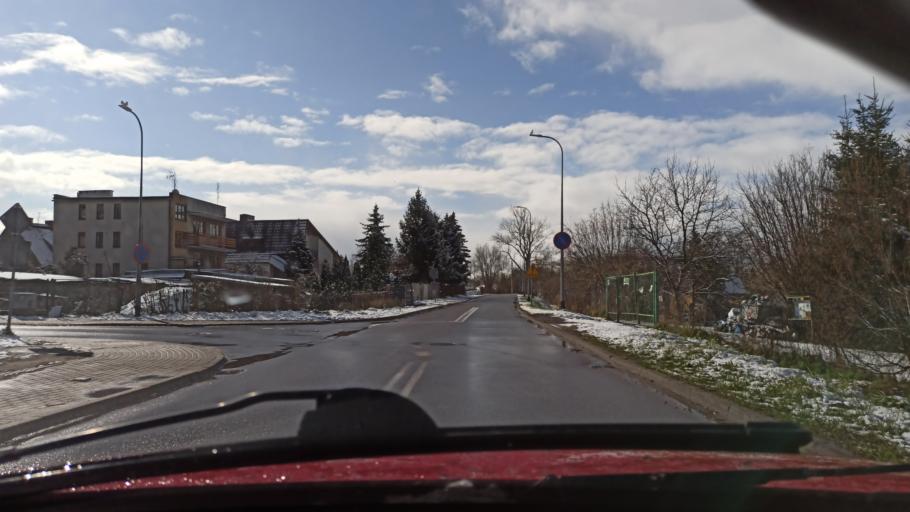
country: PL
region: Warmian-Masurian Voivodeship
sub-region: Powiat elblaski
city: Elblag
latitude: 54.1459
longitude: 19.4037
